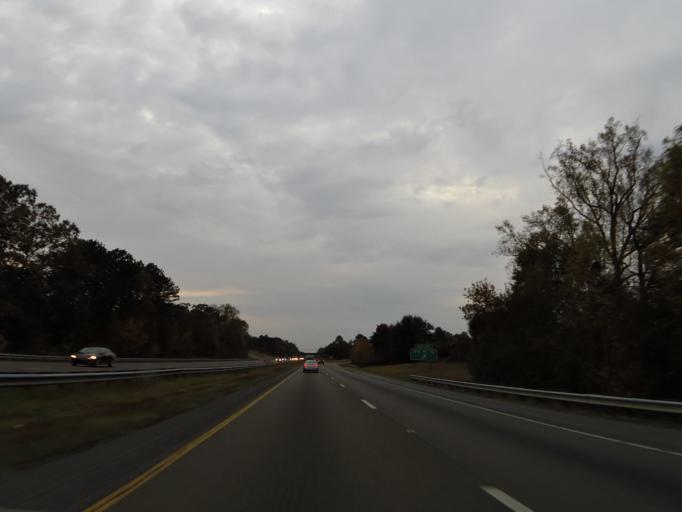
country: US
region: North Carolina
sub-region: Burke County
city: Hildebran
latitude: 35.7080
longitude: -81.4344
